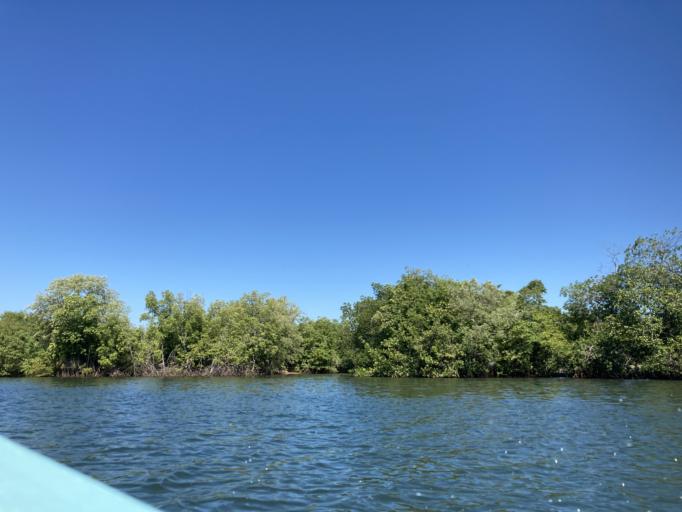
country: GT
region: Jutiapa
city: Pasaco
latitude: 13.8098
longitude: -90.2726
